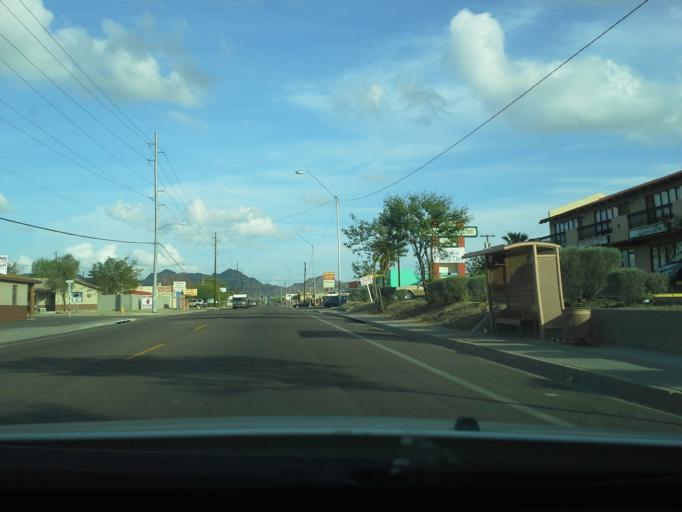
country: US
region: Arizona
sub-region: Maricopa County
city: Glendale
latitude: 33.5713
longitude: -112.0787
